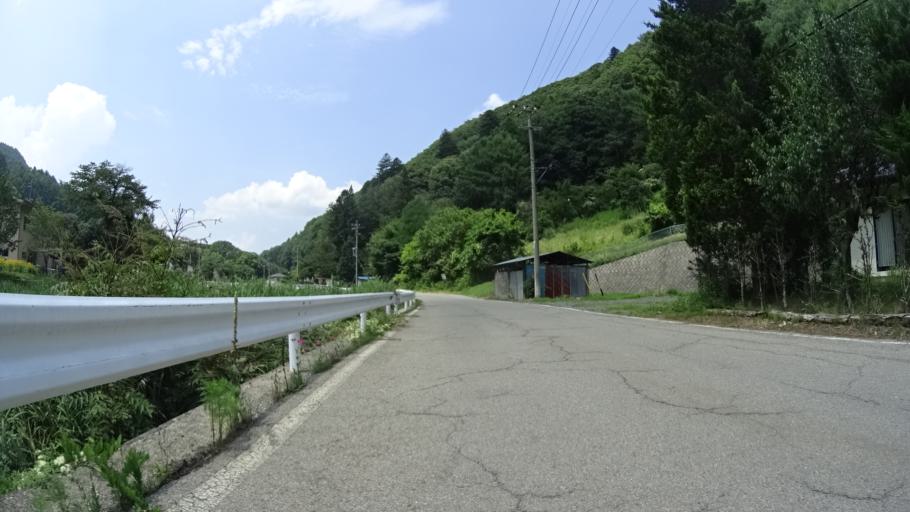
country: JP
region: Nagano
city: Saku
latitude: 36.1288
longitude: 138.5799
